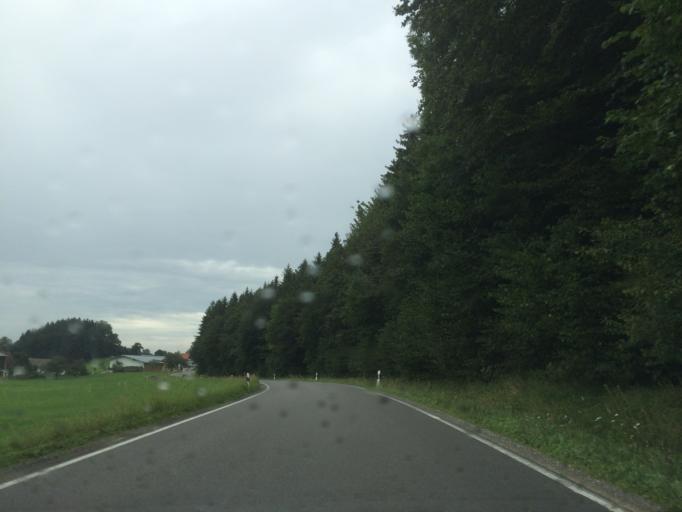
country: DE
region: Baden-Wuerttemberg
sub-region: Tuebingen Region
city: Bad Waldsee
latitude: 47.9479
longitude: 9.7767
